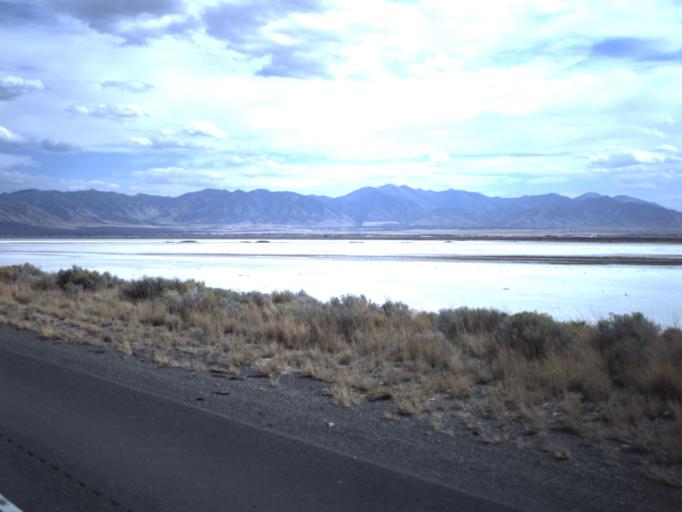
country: US
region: Utah
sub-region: Tooele County
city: Grantsville
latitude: 40.6812
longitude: -112.4267
